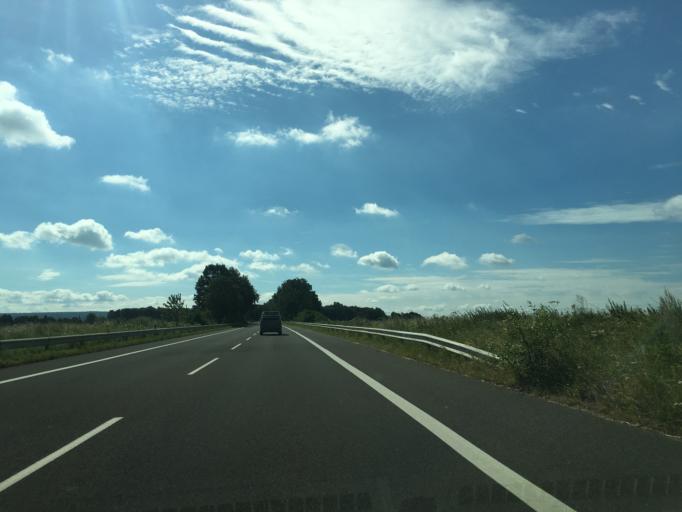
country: DE
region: North Rhine-Westphalia
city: Julich
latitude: 50.9698
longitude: 6.3570
